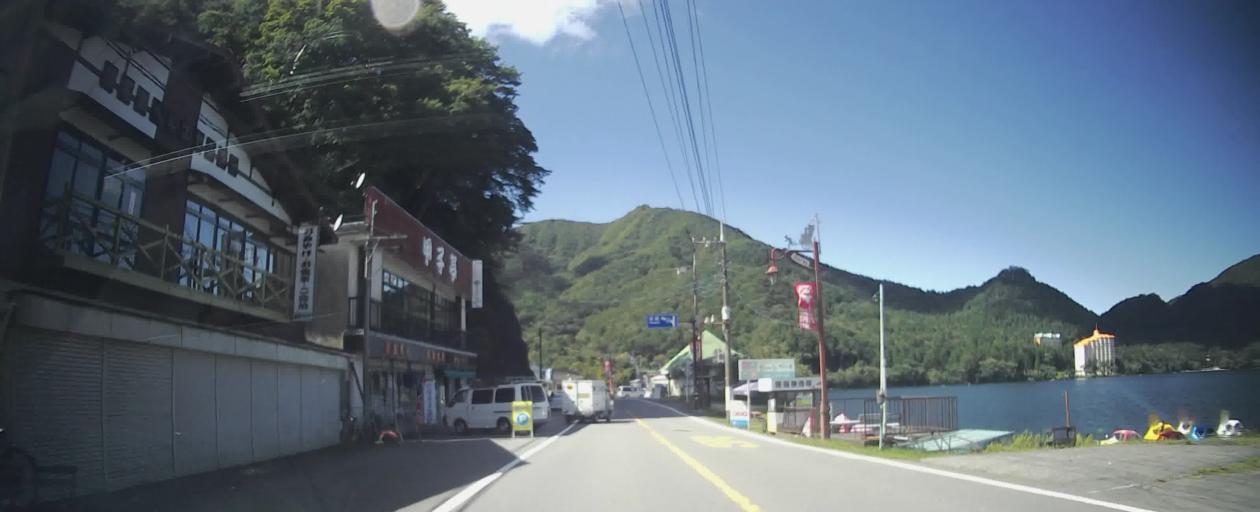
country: JP
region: Gunma
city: Nakanojomachi
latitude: 36.4676
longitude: 138.8632
